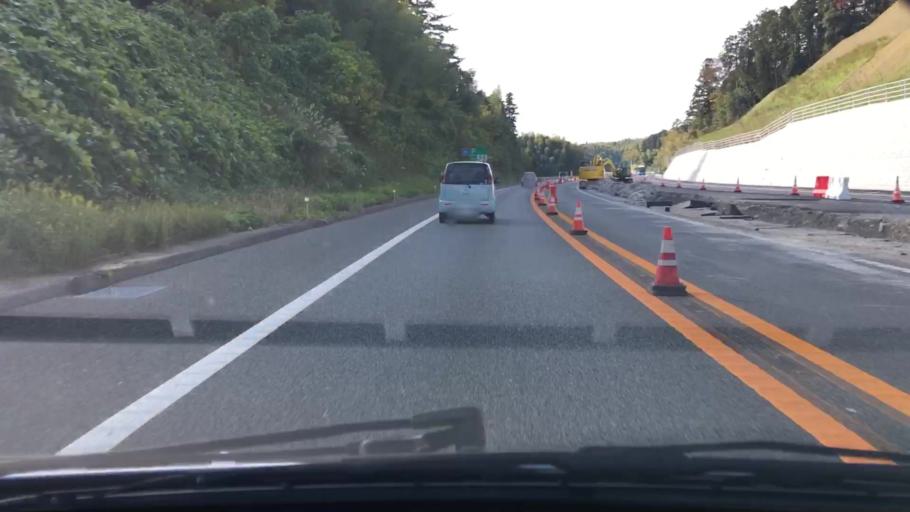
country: JP
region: Chiba
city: Kimitsu
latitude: 35.3002
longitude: 139.9393
